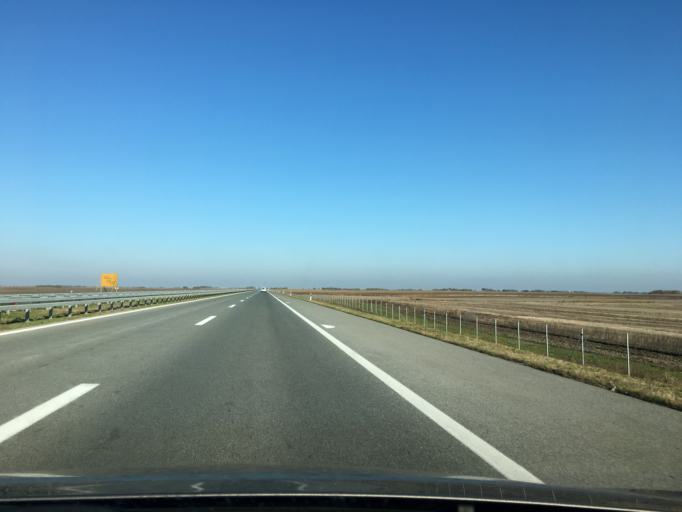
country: RS
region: Autonomna Pokrajina Vojvodina
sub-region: Severnobacki Okrug
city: Mali Igos
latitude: 45.7556
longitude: 19.7019
